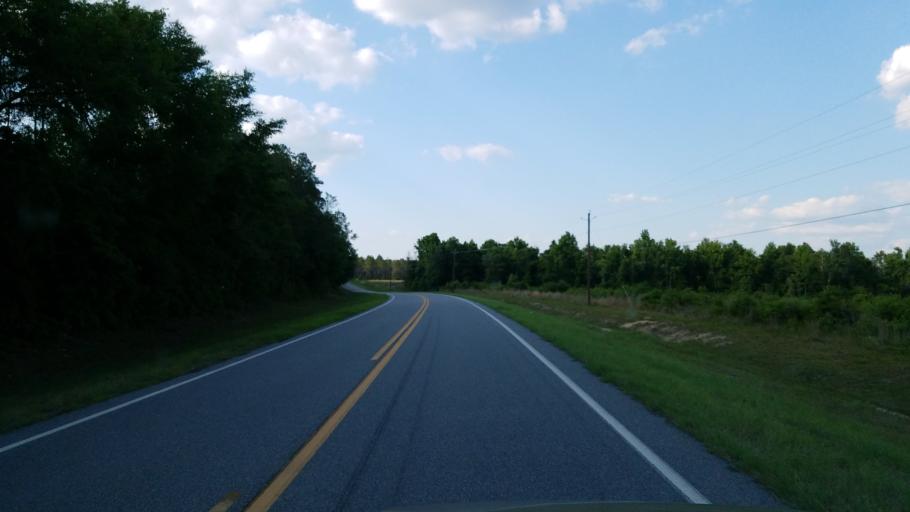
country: US
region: Georgia
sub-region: Echols County
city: Statenville
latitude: 30.7205
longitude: -83.0570
